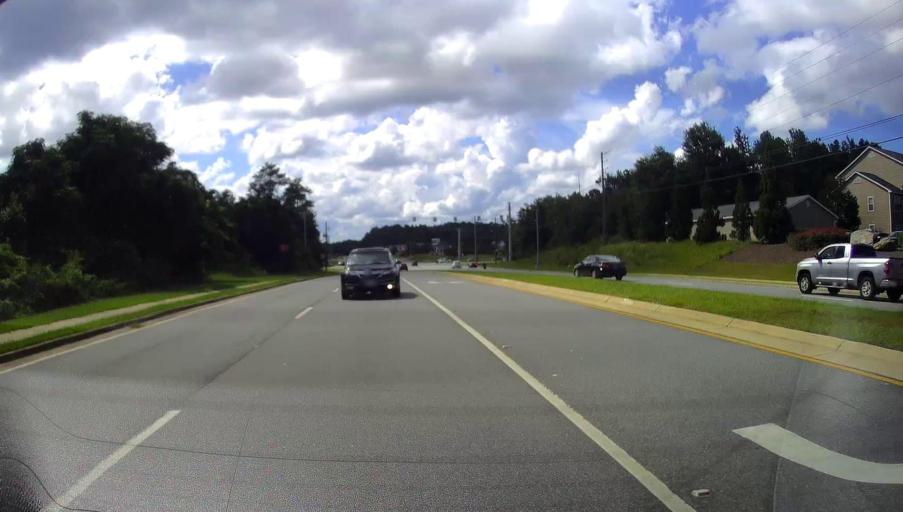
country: US
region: Alabama
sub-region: Russell County
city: Phenix City
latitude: 32.5619
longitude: -84.9353
